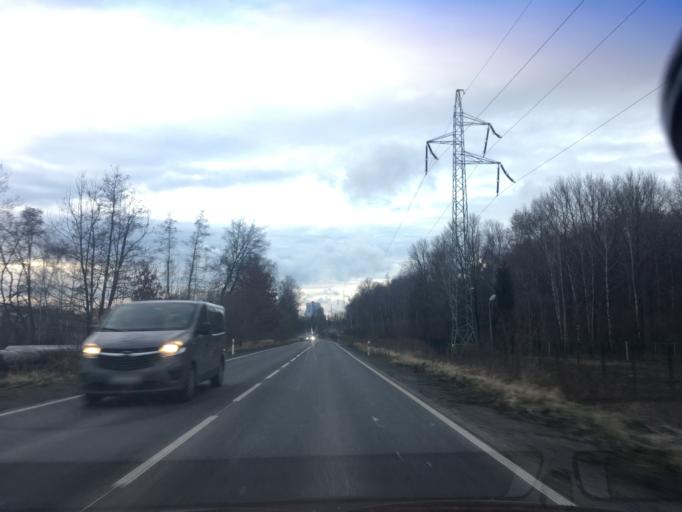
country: PL
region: Lower Silesian Voivodeship
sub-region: Powiat zgorzelecki
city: Bogatynia
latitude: 50.9319
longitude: 14.9245
